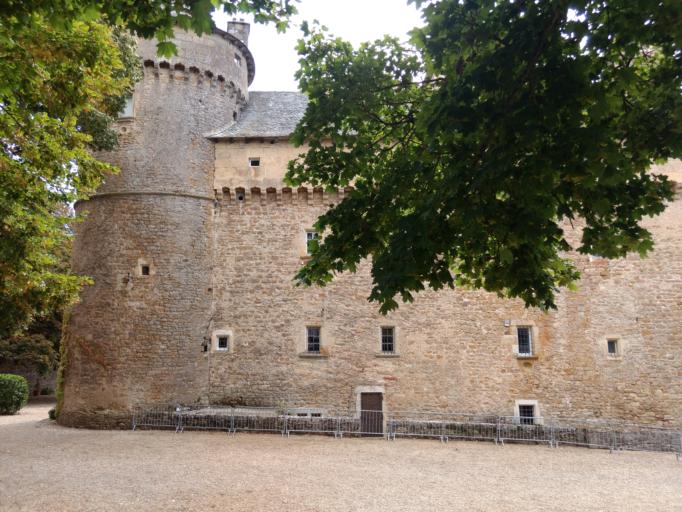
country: FR
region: Midi-Pyrenees
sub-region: Departement de l'Aveyron
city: Bozouls
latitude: 44.4064
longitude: 2.7462
